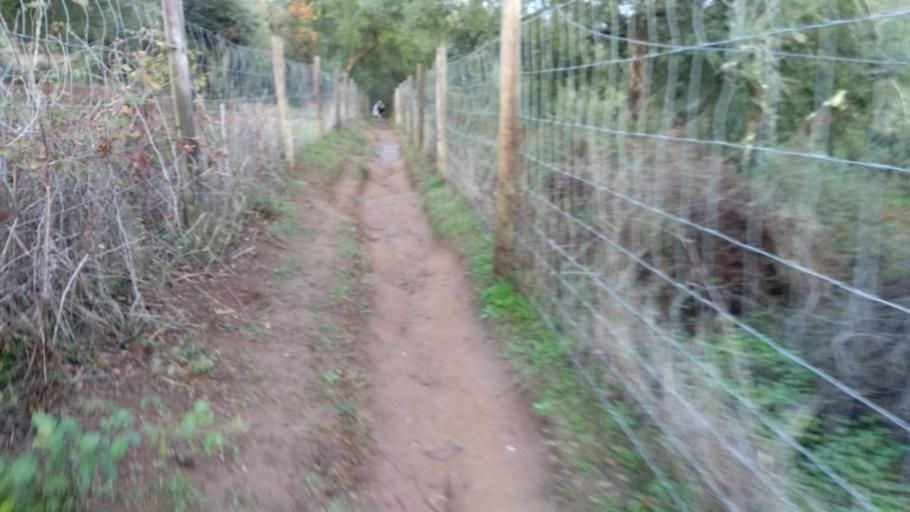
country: PT
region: Evora
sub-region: Evora
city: Evora
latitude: 38.5641
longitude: -8.0480
